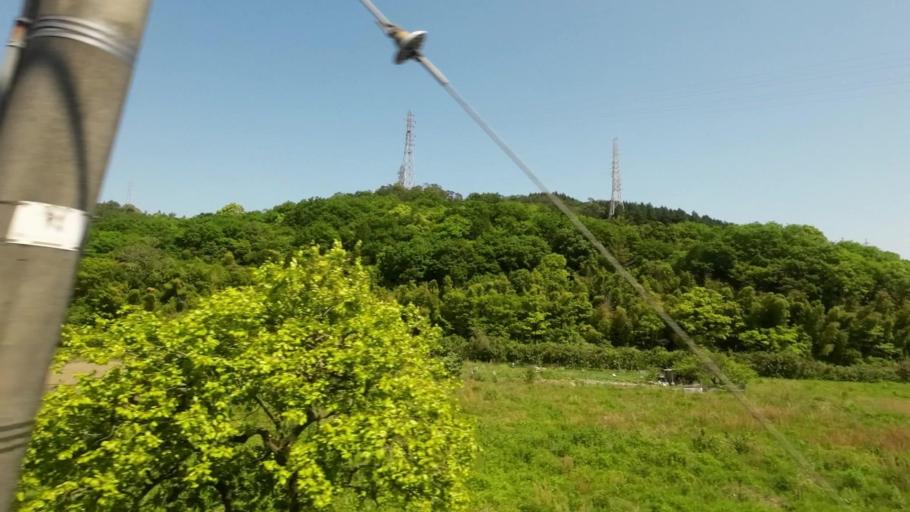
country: JP
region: Ehime
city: Niihama
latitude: 33.9364
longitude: 133.2772
